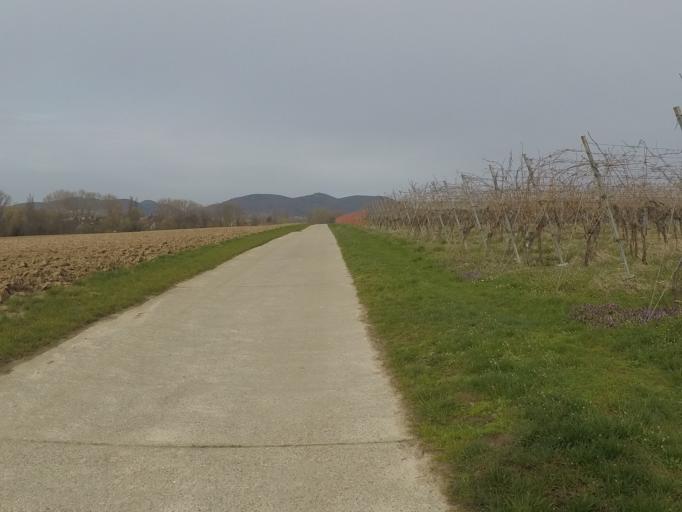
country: DE
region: Rheinland-Pfalz
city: Heuchelheim-Klingen
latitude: 49.1395
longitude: 8.0714
